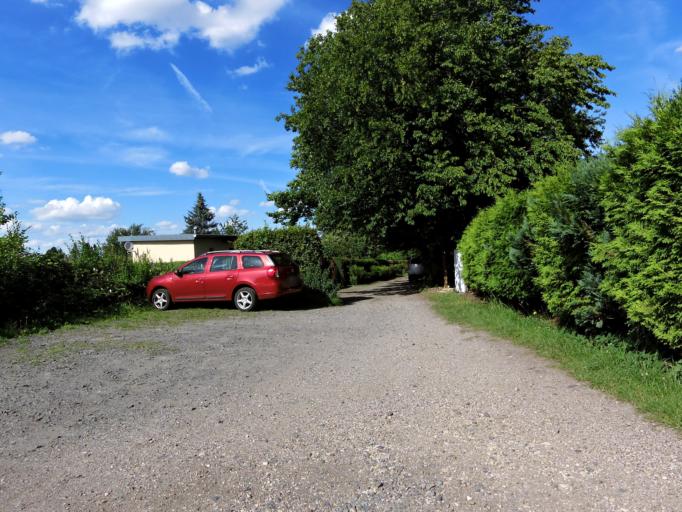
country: DE
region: Saxony
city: Leipzig
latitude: 51.3183
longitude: 12.4390
